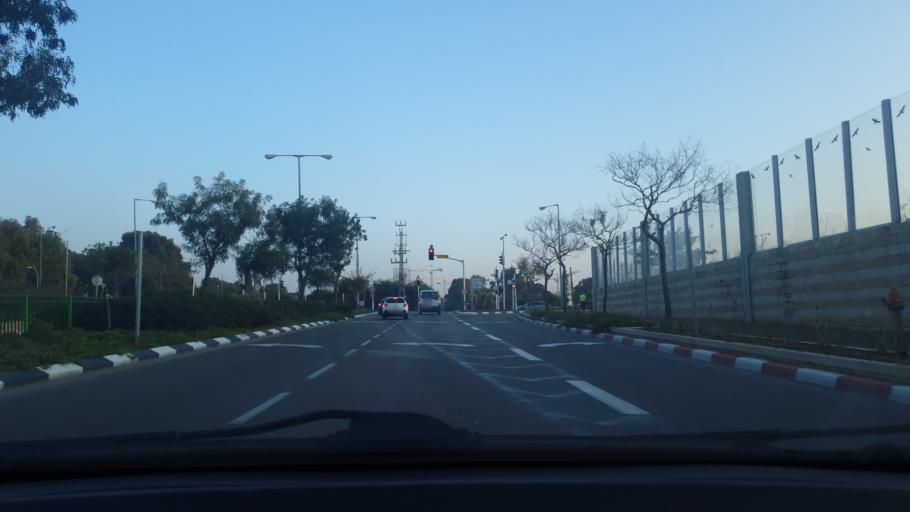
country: IL
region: Central District
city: Bet Dagan
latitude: 31.9686
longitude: 34.8265
